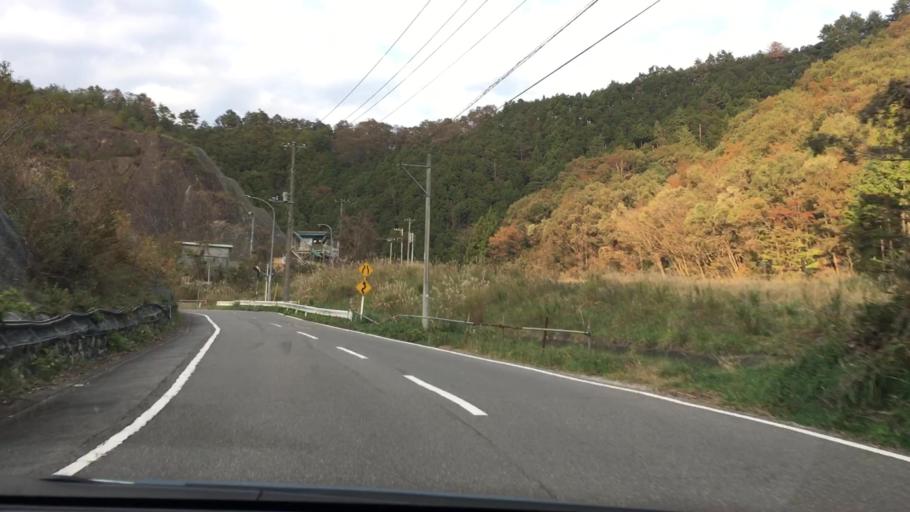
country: JP
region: Yamanashi
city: Uenohara
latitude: 35.5566
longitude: 139.1392
